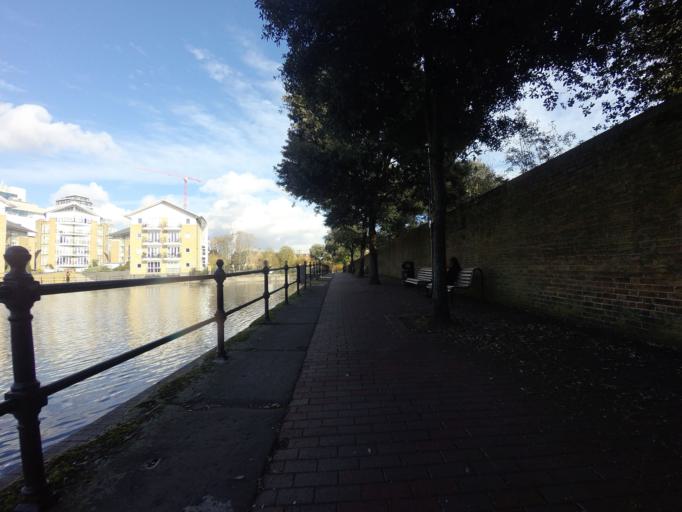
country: GB
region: England
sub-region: Greater London
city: Bethnal Green
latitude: 51.5053
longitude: -0.0672
